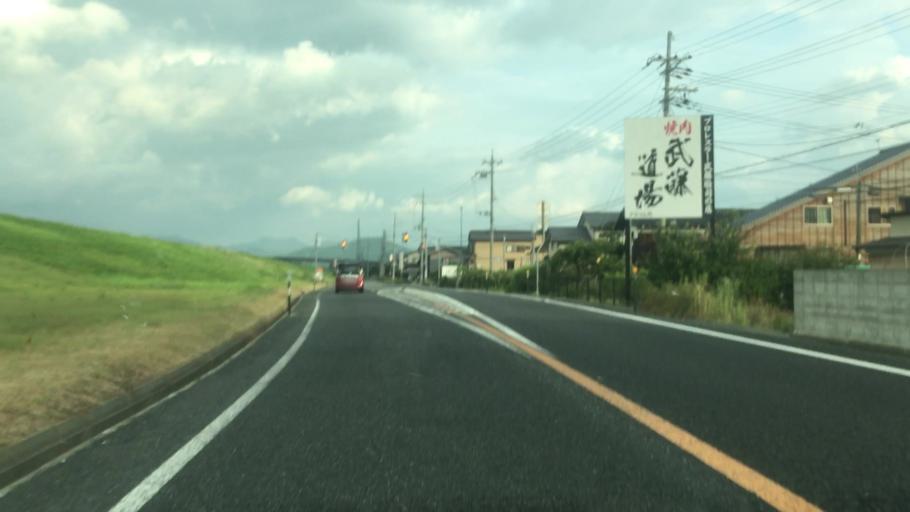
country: JP
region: Hyogo
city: Toyooka
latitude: 35.5593
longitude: 134.8154
